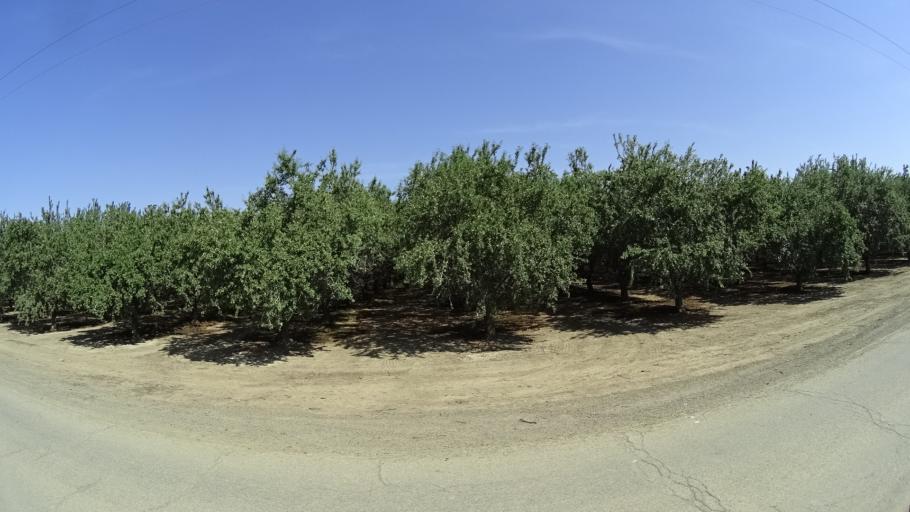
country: US
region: California
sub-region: Kings County
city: Kettleman City
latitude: 36.0942
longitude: -120.0009
